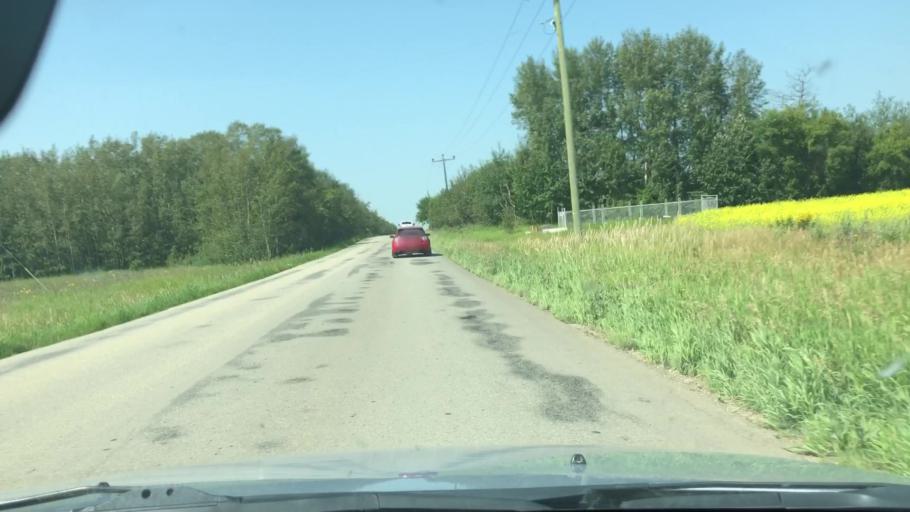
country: CA
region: Alberta
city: Devon
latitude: 53.5122
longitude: -113.7246
